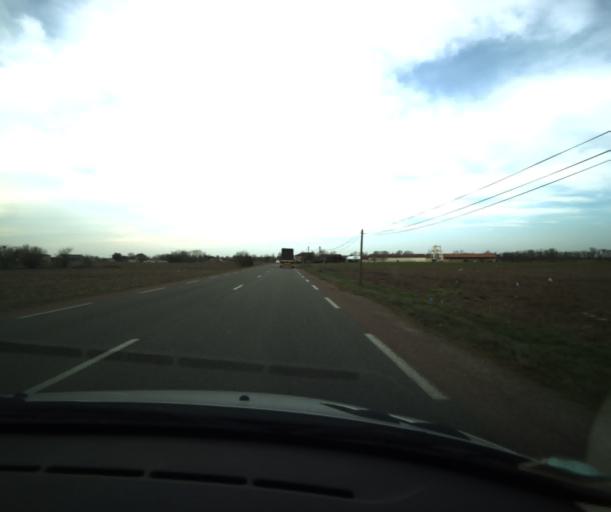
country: FR
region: Midi-Pyrenees
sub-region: Departement du Tarn-et-Garonne
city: Saint-Porquier
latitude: 43.9933
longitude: 1.1896
